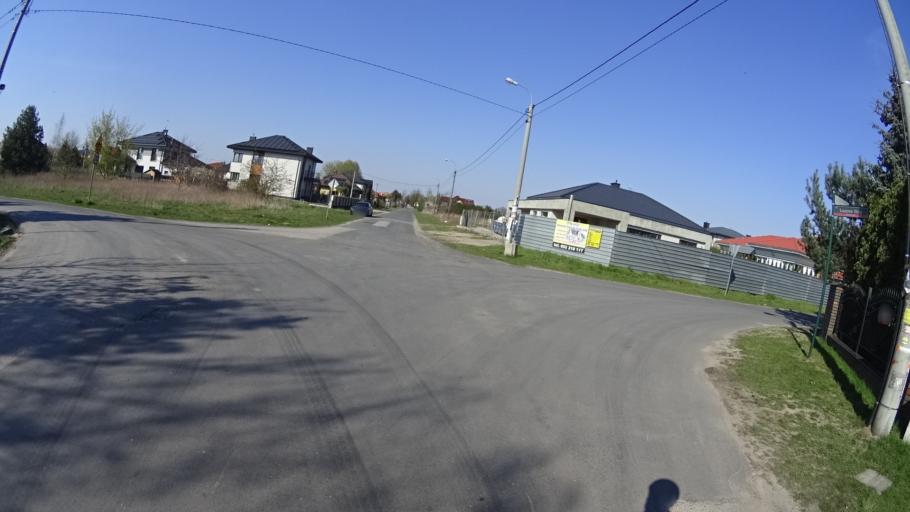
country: PL
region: Masovian Voivodeship
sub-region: Powiat warszawski zachodni
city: Babice
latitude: 52.2571
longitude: 20.8441
